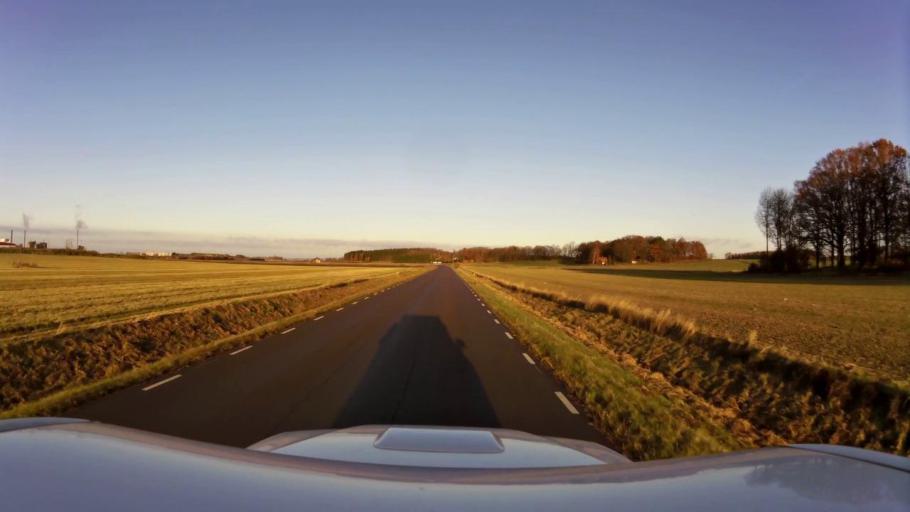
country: SE
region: OEstergoetland
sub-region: Linkopings Kommun
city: Ekangen
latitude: 58.4382
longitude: 15.6778
